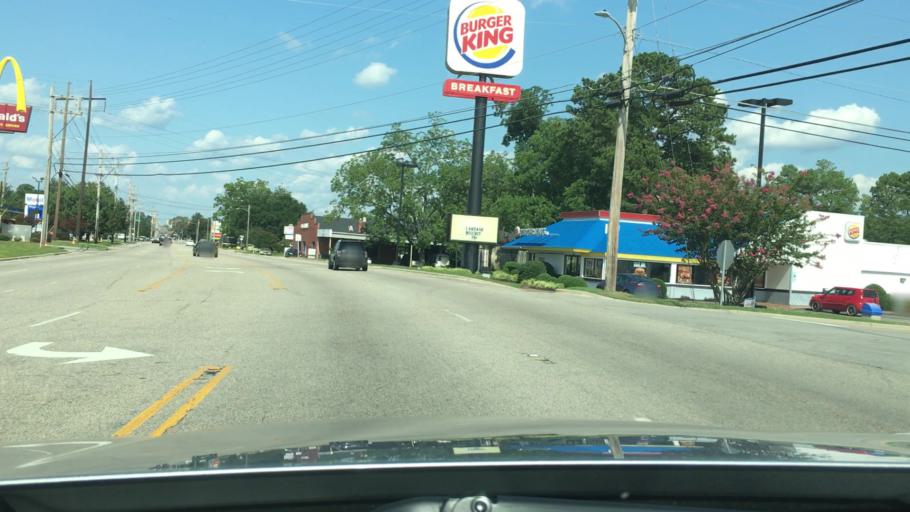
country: US
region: North Carolina
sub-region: Robeson County
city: Lumberton
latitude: 34.6222
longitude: -79.0492
